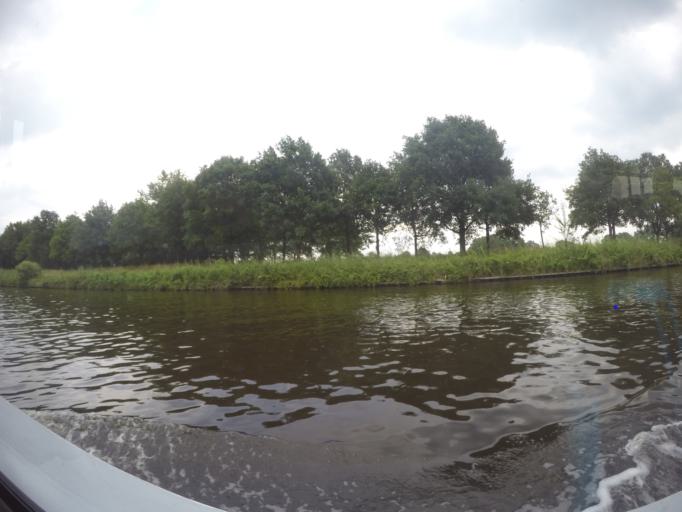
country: NL
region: Overijssel
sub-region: Gemeente Hof van Twente
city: Hengevelde
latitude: 52.2612
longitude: 6.6460
